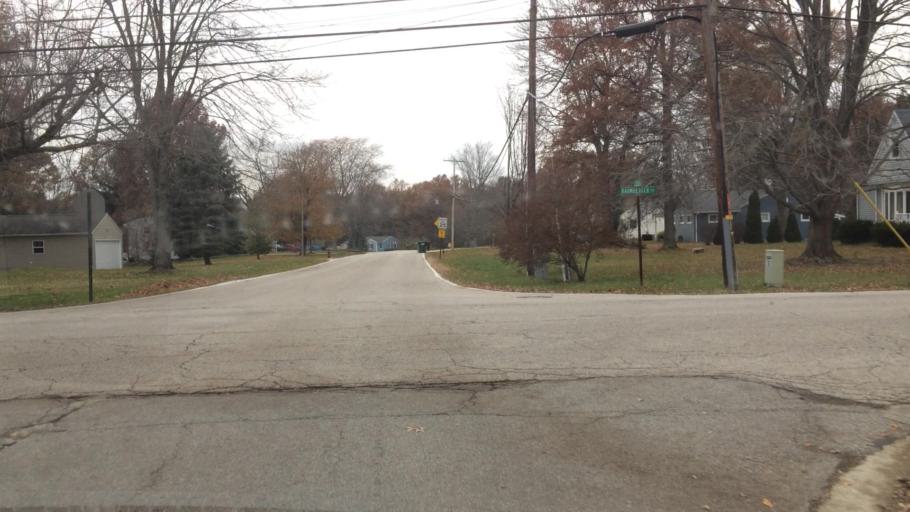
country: US
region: Ohio
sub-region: Summit County
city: Silver Lake
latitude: 41.1769
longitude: -81.4548
